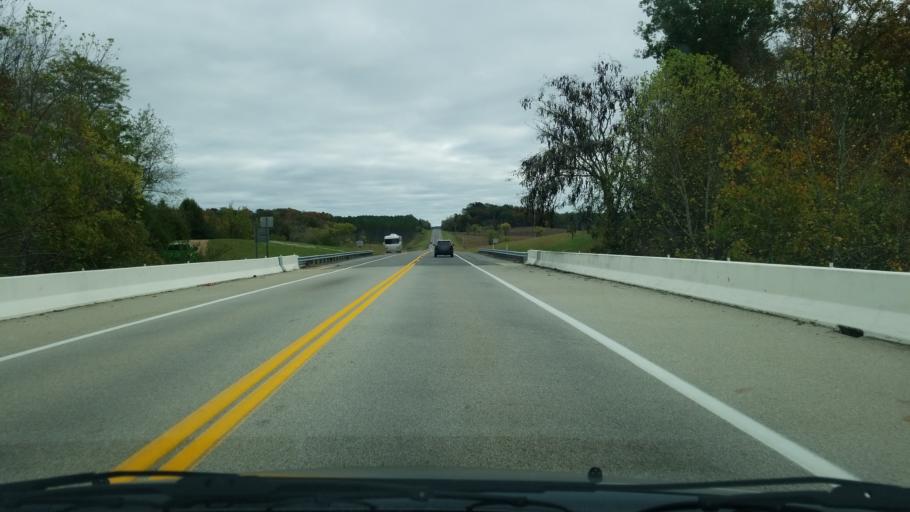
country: US
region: Tennessee
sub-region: Rhea County
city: Graysville
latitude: 35.4068
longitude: -85.0173
